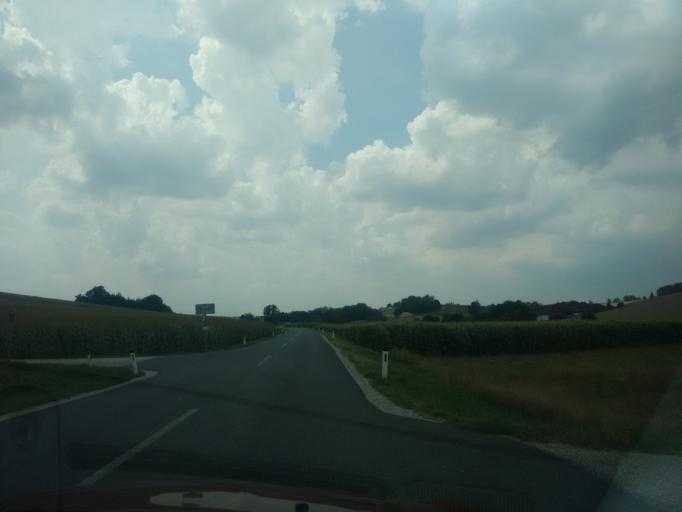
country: AT
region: Upper Austria
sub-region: Politischer Bezirk Grieskirchen
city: Bad Schallerbach
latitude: 48.2620
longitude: 13.9185
